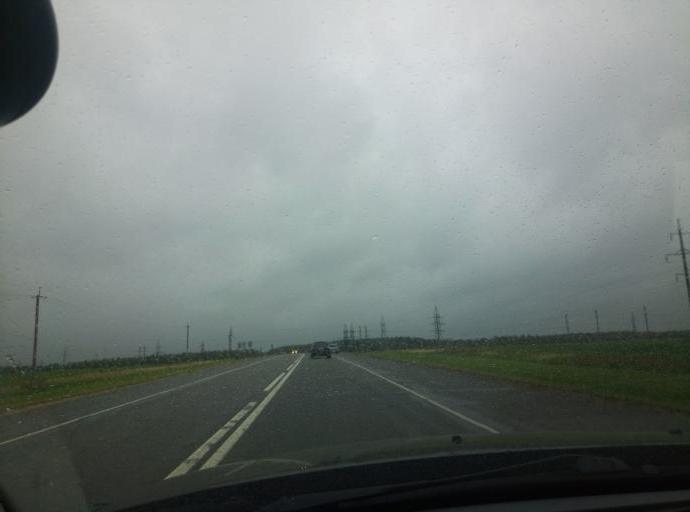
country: RU
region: Tula
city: Barsuki
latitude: 54.2599
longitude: 37.5312
